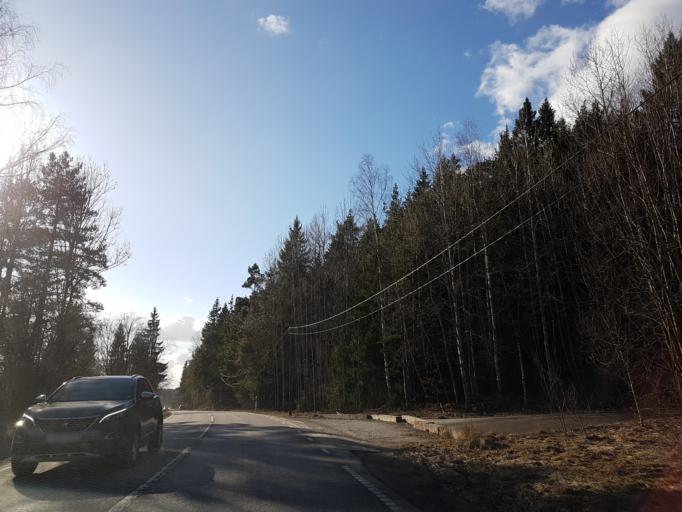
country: SE
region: Stockholm
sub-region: Norrtalje Kommun
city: Rimbo
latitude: 59.7348
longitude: 18.4437
